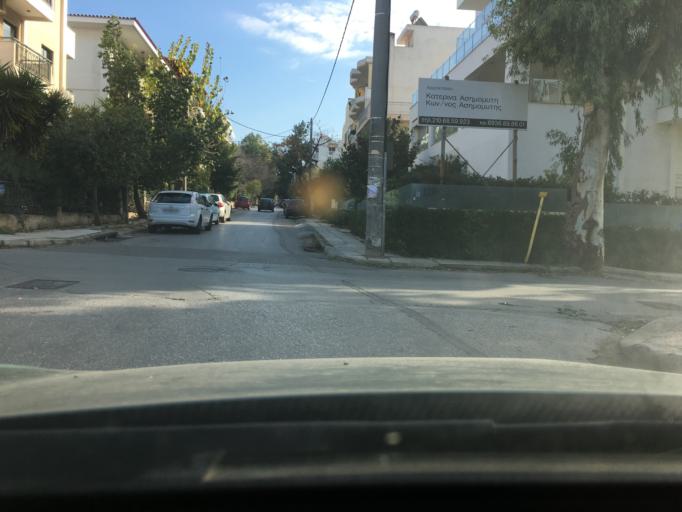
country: GR
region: Attica
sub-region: Nomarchia Athinas
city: Khalandrion
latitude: 38.0277
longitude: 23.7974
